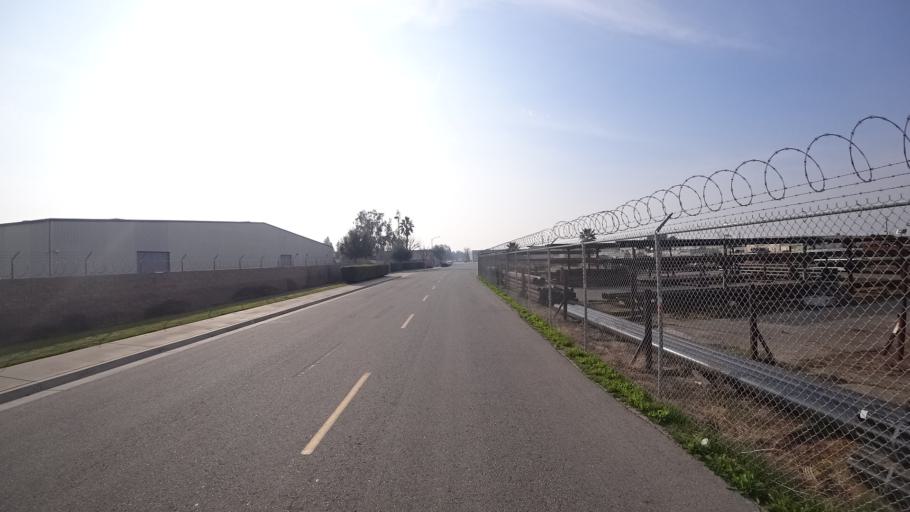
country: US
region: California
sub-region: Kern County
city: Bakersfield
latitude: 35.3917
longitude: -119.0388
